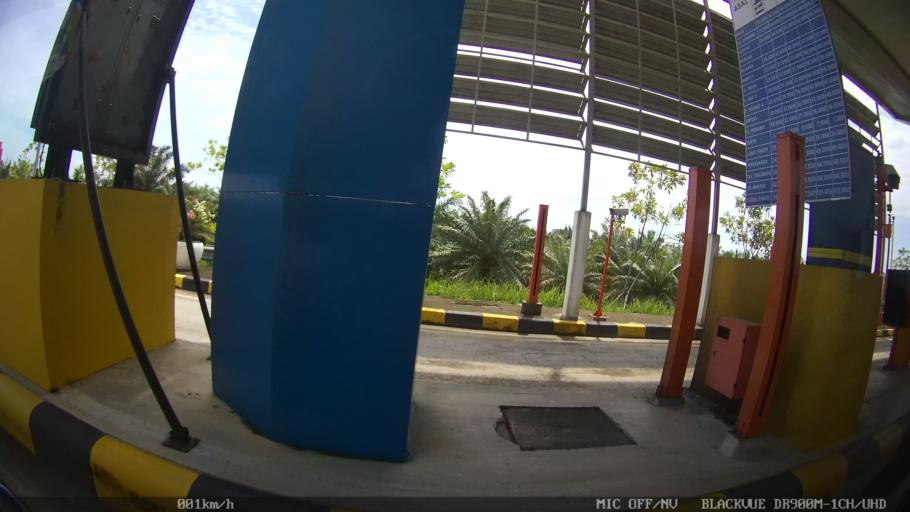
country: ID
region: North Sumatra
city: Percut
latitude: 3.5889
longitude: 98.8449
